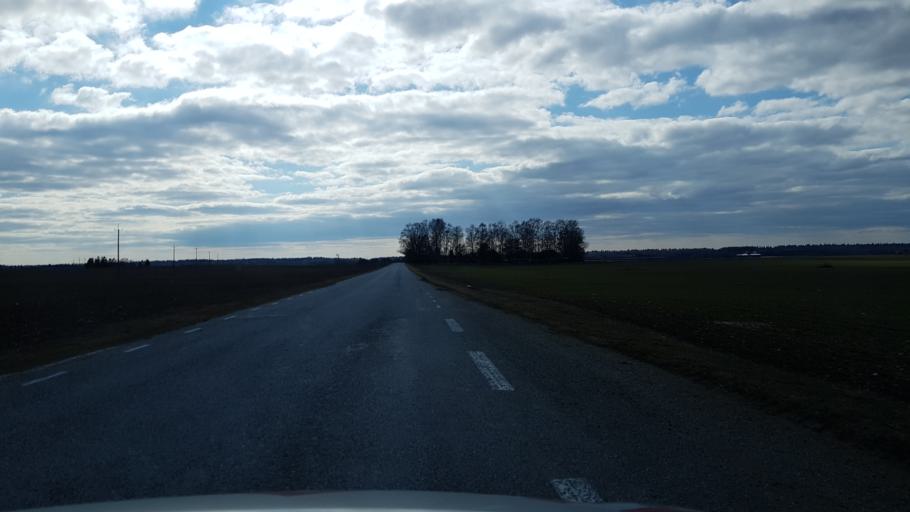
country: EE
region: Laeaene-Virumaa
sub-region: Kadrina vald
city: Kadrina
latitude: 59.2945
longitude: 26.2075
